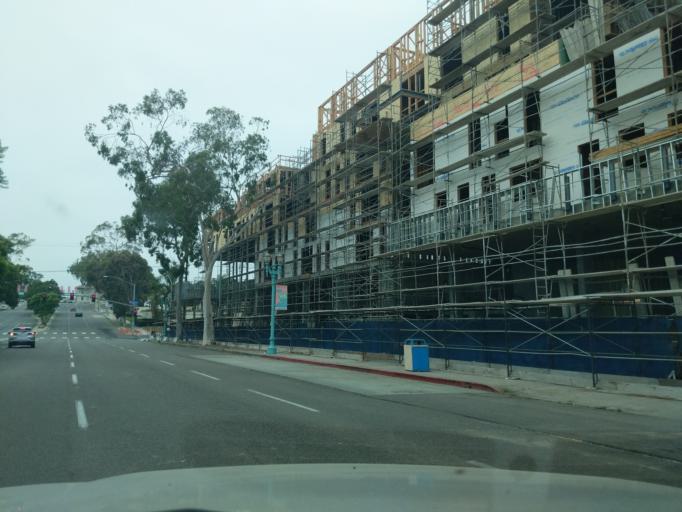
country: US
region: California
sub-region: San Diego County
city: San Diego
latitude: 32.7554
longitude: -117.1427
